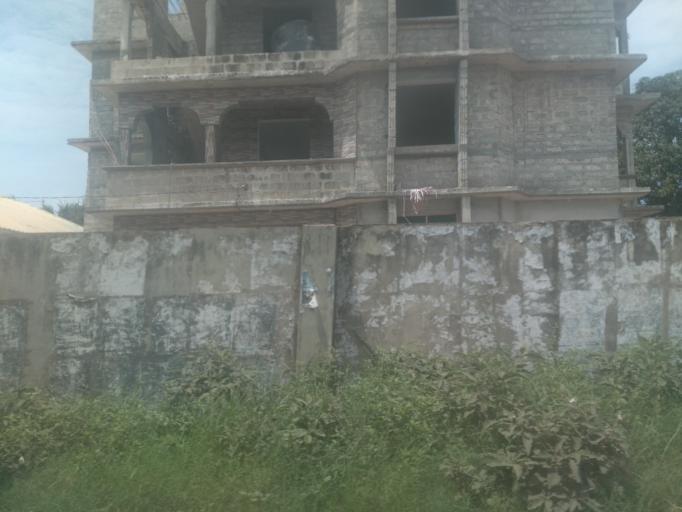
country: TZ
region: Zanzibar Urban/West
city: Zanzibar
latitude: -6.2237
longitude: 39.2139
